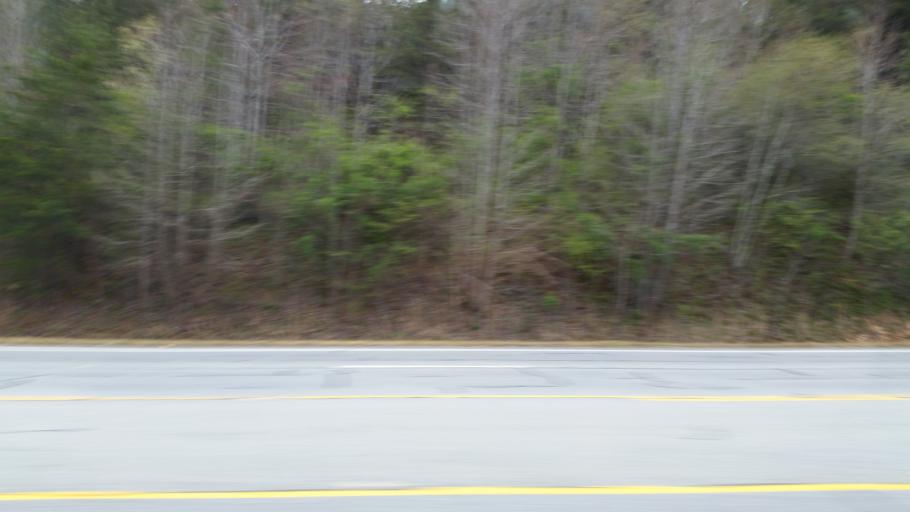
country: US
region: Georgia
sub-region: Fannin County
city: Blue Ridge
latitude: 34.8433
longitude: -84.3358
